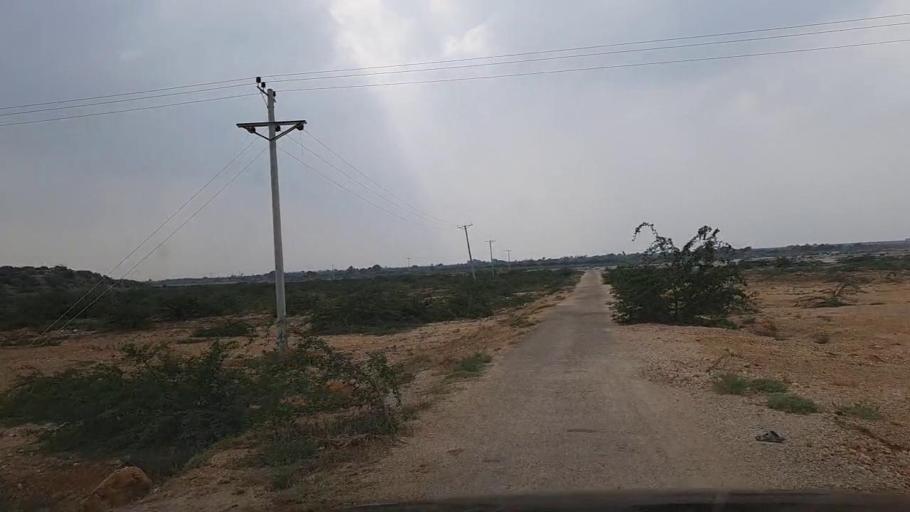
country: PK
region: Sindh
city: Thatta
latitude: 24.8272
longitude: 67.8234
